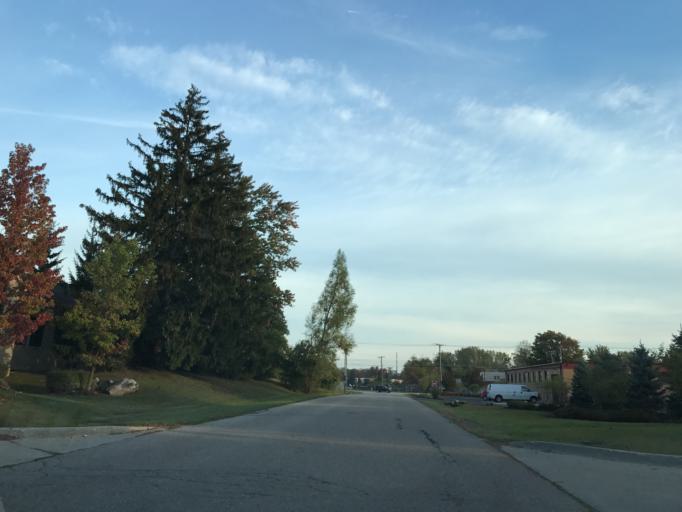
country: US
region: Michigan
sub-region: Oakland County
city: Novi
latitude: 42.4819
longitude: -83.4873
